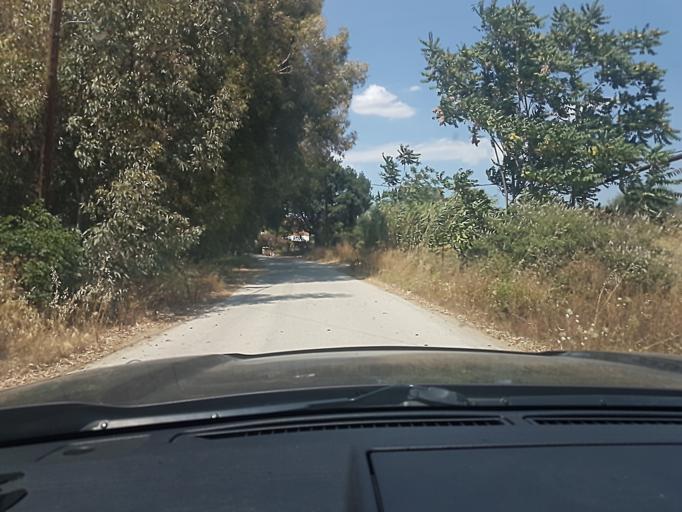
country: GR
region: Central Greece
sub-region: Nomos Evvoias
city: Vasilikon
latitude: 38.4203
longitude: 23.6623
